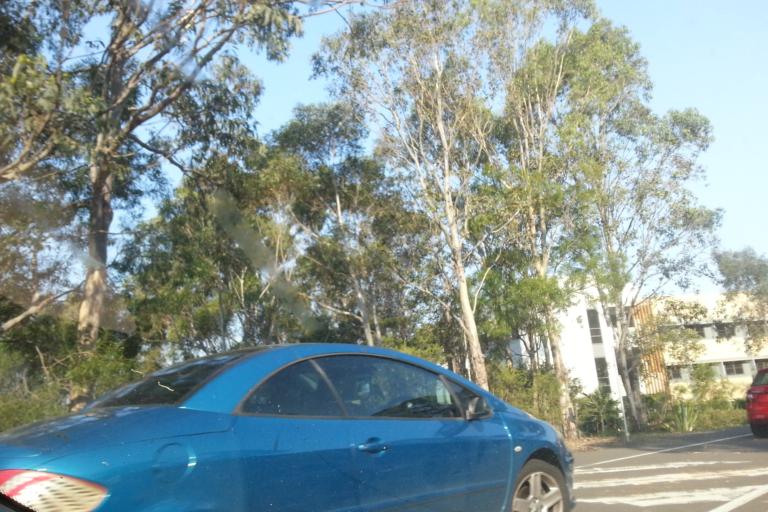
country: AU
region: New South Wales
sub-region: Wollongong
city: Mount Ousley
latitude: -34.4051
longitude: 150.8729
